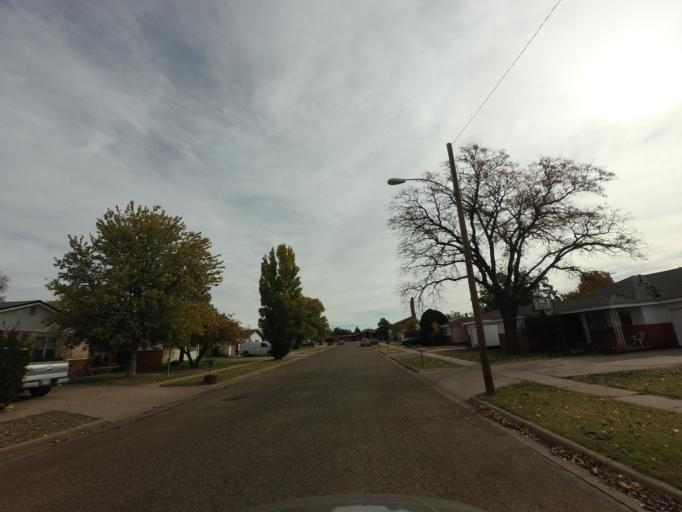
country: US
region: New Mexico
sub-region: Curry County
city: Clovis
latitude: 34.4246
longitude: -103.2086
